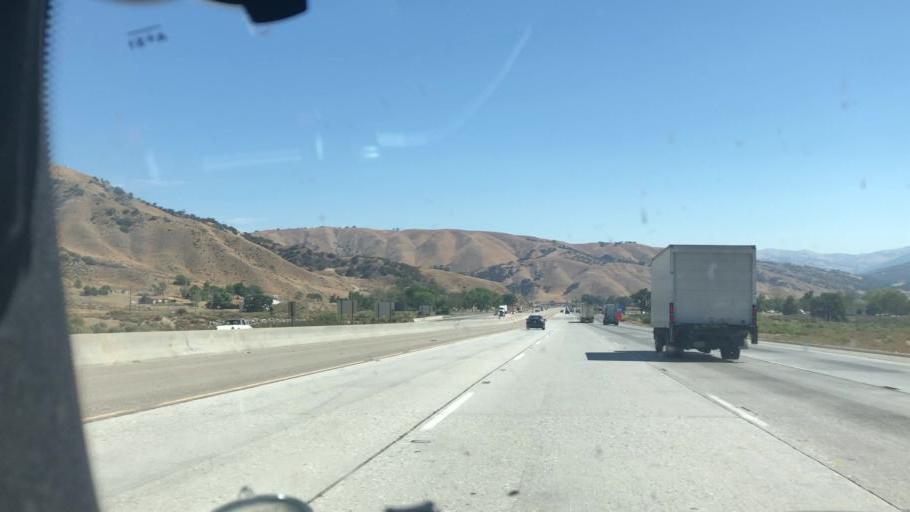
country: US
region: California
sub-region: Kern County
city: Lebec
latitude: 34.8233
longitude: -118.8778
